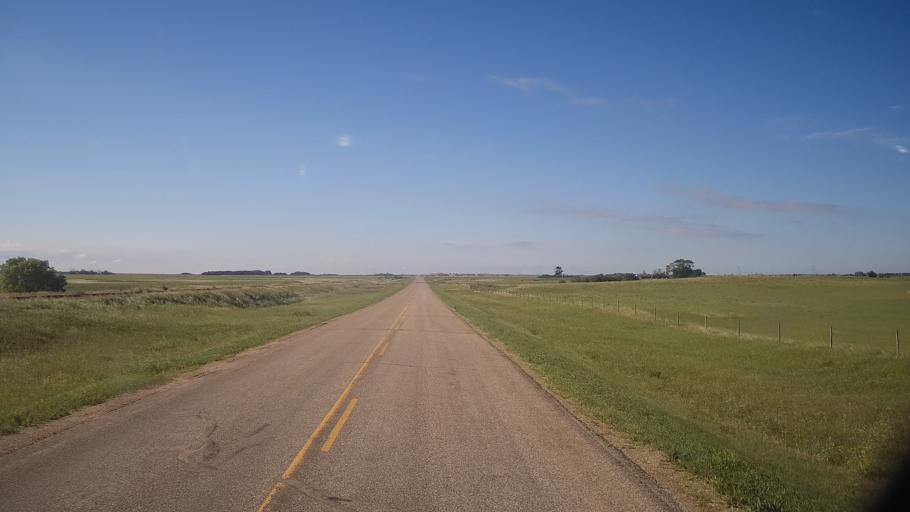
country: CA
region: Saskatchewan
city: Watrous
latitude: 51.7462
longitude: -105.2867
